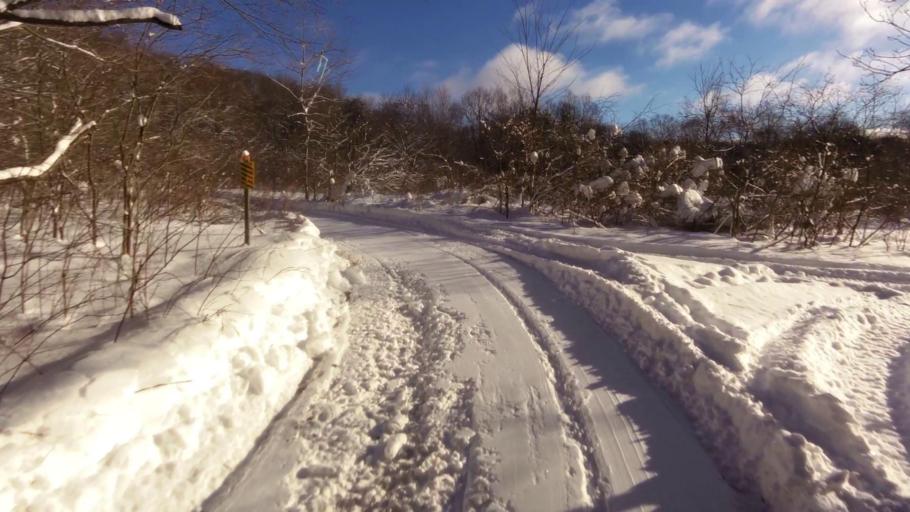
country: US
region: New York
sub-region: Chautauqua County
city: Falconer
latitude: 42.2557
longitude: -79.1653
